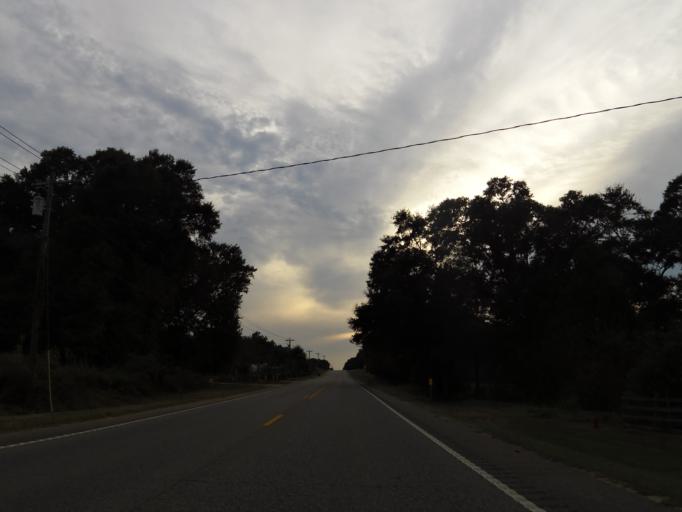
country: US
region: Alabama
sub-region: Escambia County
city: Atmore
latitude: 31.0053
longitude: -87.5807
